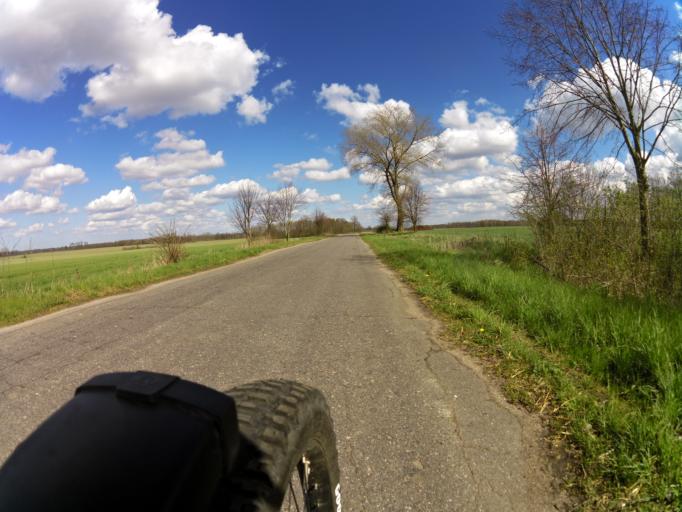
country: PL
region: West Pomeranian Voivodeship
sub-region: Powiat gryficki
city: Ploty
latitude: 53.8392
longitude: 15.2012
